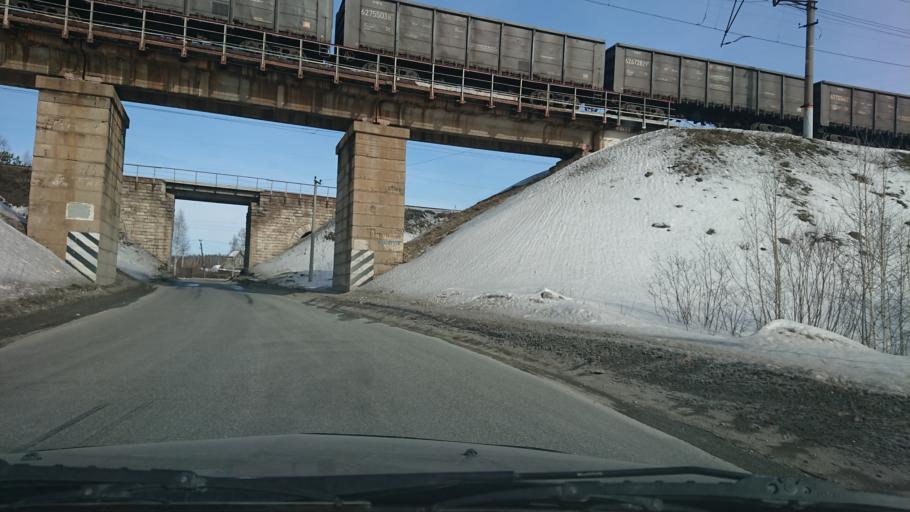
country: RU
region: Sverdlovsk
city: Revda
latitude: 56.8206
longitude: 59.9776
